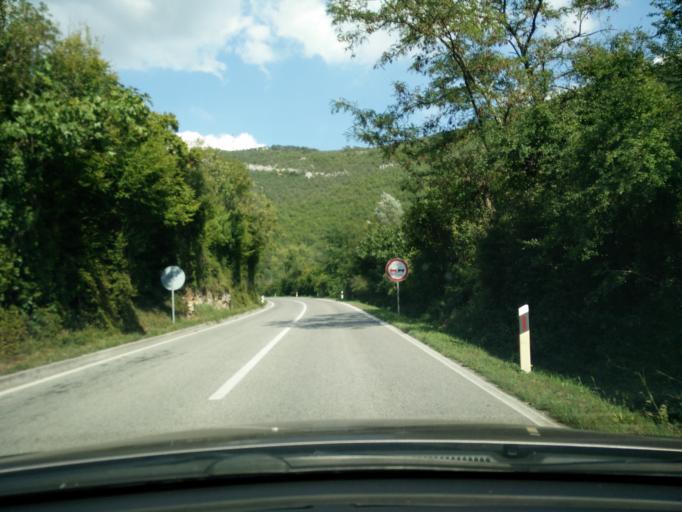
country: HR
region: Istarska
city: Buzet
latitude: 45.3811
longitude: 13.8939
